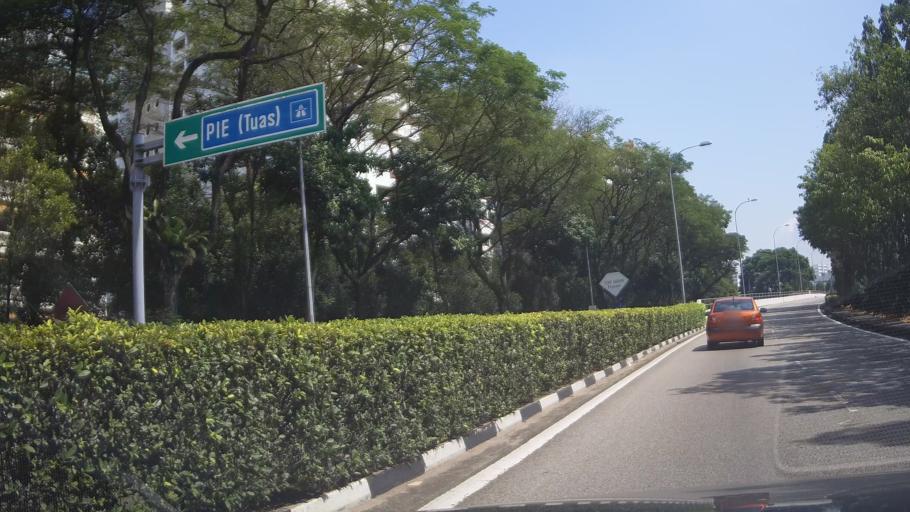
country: SG
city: Singapore
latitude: 1.3392
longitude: 103.7476
